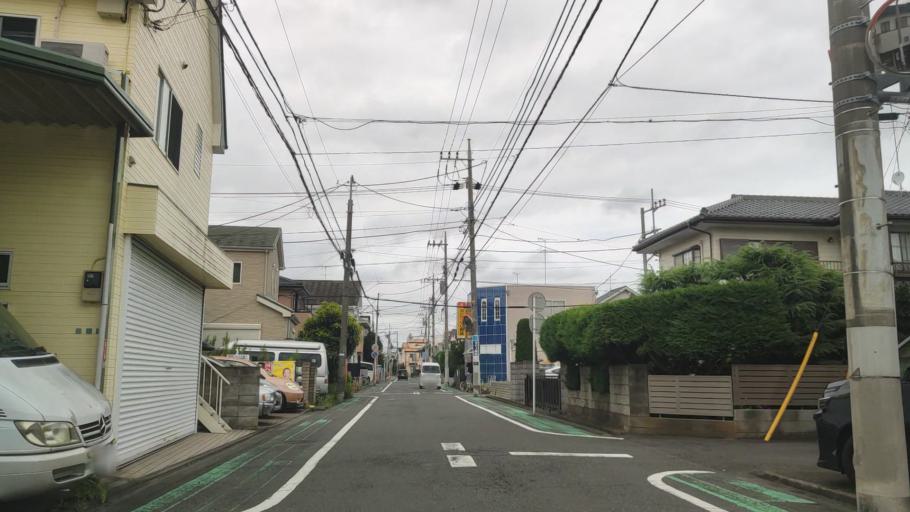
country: JP
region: Tokyo
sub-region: Machida-shi
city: Machida
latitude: 35.5156
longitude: 139.4360
